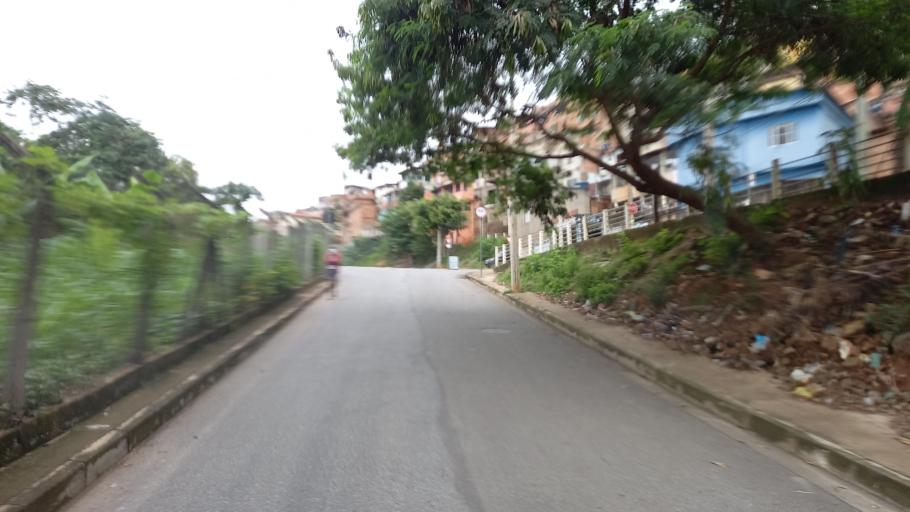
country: BR
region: Minas Gerais
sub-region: Belo Horizonte
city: Belo Horizonte
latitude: -19.9107
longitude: -43.8882
